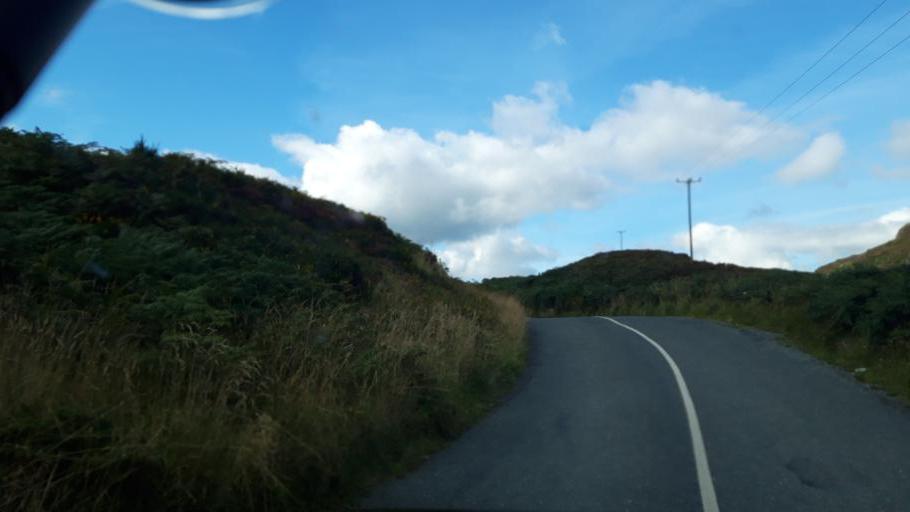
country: GB
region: Northern Ireland
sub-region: Down District
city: Warrenpoint
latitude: 54.0589
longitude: -6.2736
